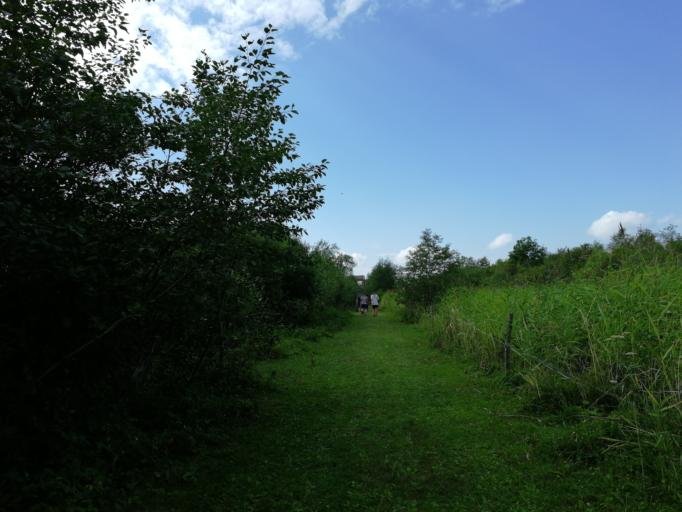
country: EE
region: Laeaene
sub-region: Lihula vald
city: Lihula
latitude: 58.7263
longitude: 23.8057
